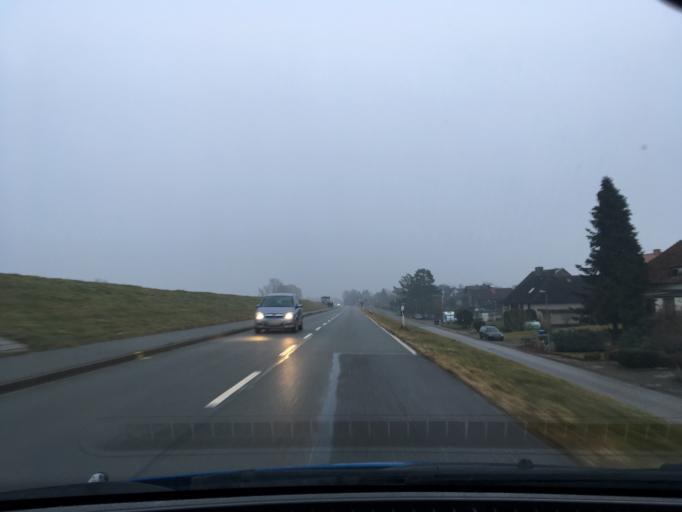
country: DE
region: Hamburg
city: Harburg
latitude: 53.4589
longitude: 10.0564
